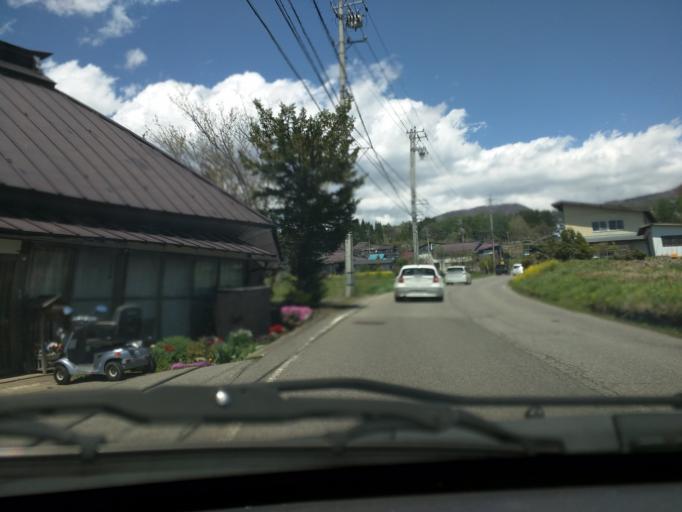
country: JP
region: Nagano
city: Nagano-shi
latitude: 36.7080
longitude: 138.0909
